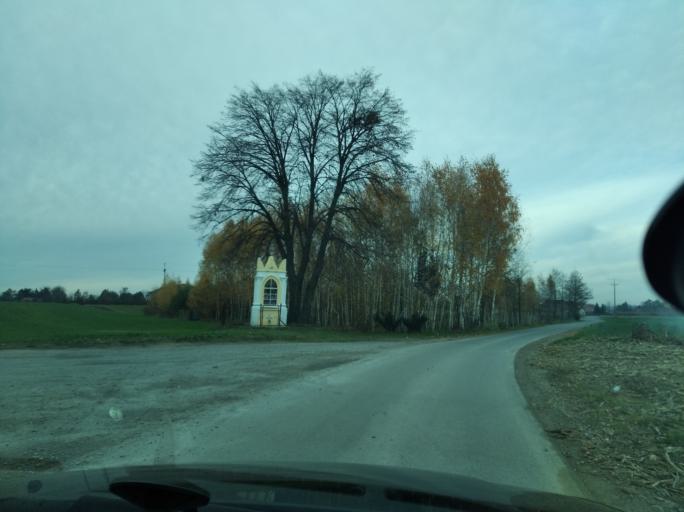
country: PL
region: Subcarpathian Voivodeship
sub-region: Powiat przeworski
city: Grzeska
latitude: 50.0708
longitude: 22.4576
